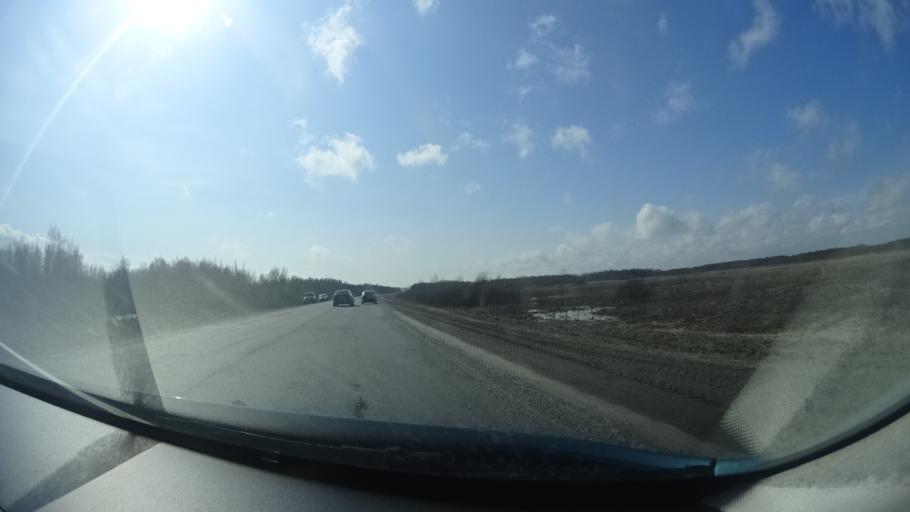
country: RU
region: Bashkortostan
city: Mikhaylovka
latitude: 54.9156
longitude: 55.7347
